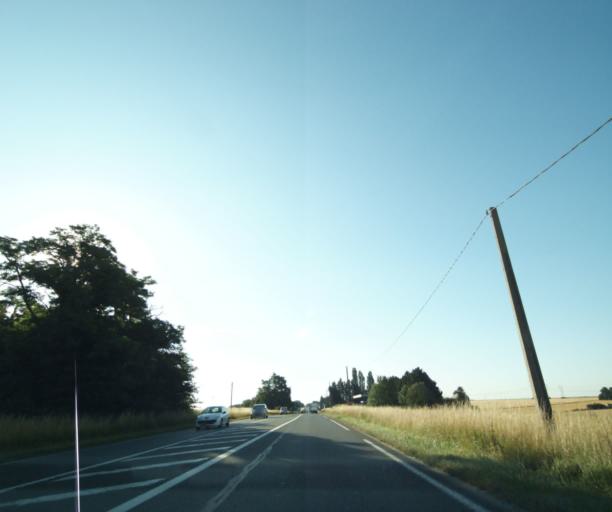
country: FR
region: Ile-de-France
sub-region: Departement de Seine-et-Marne
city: Vernou-la-Celle-sur-Seine
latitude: 48.3652
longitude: 2.8498
